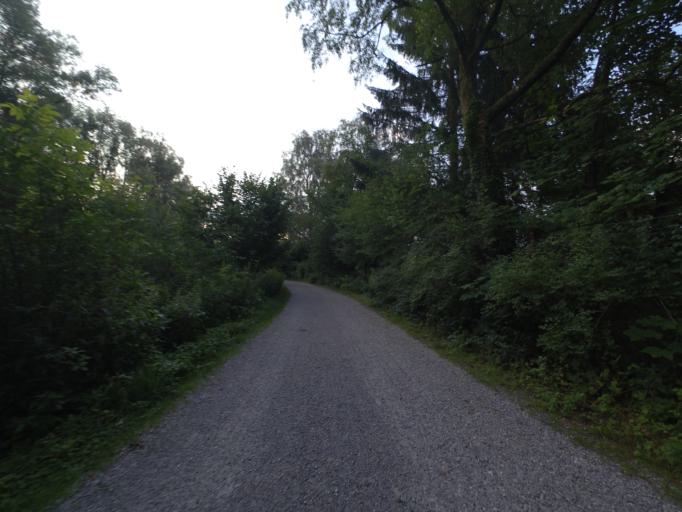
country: AT
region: Salzburg
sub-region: Politischer Bezirk Salzburg-Umgebung
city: Anif
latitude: 47.7292
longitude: 13.0728
